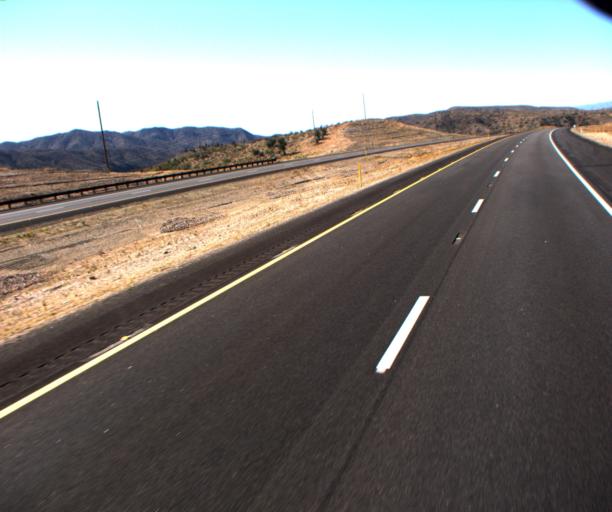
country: US
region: Arizona
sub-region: Mohave County
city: Kingman
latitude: 35.0000
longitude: -113.6644
